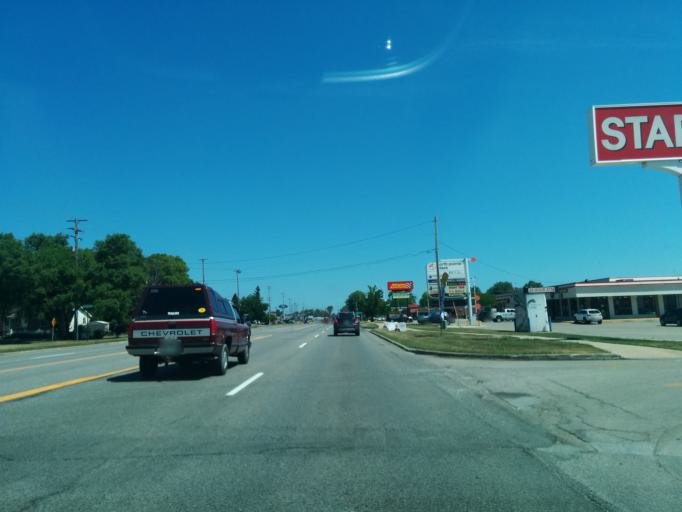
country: US
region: Michigan
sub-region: Bay County
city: Bay City
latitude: 43.6209
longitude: -83.9143
